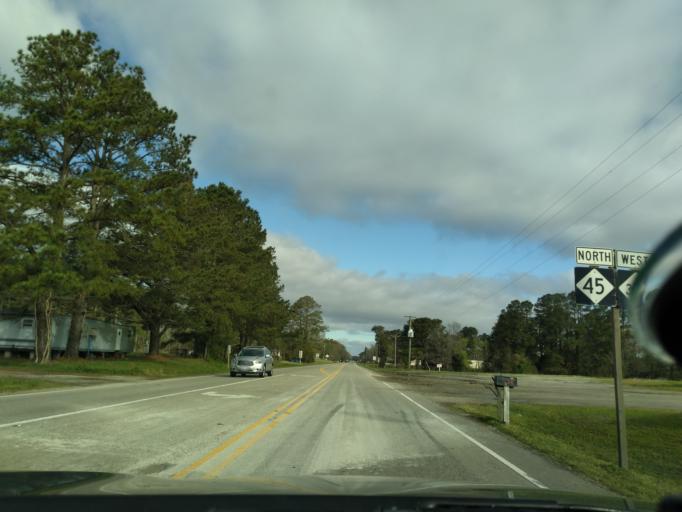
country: US
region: North Carolina
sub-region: Washington County
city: Plymouth
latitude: 35.8921
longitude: -76.7030
